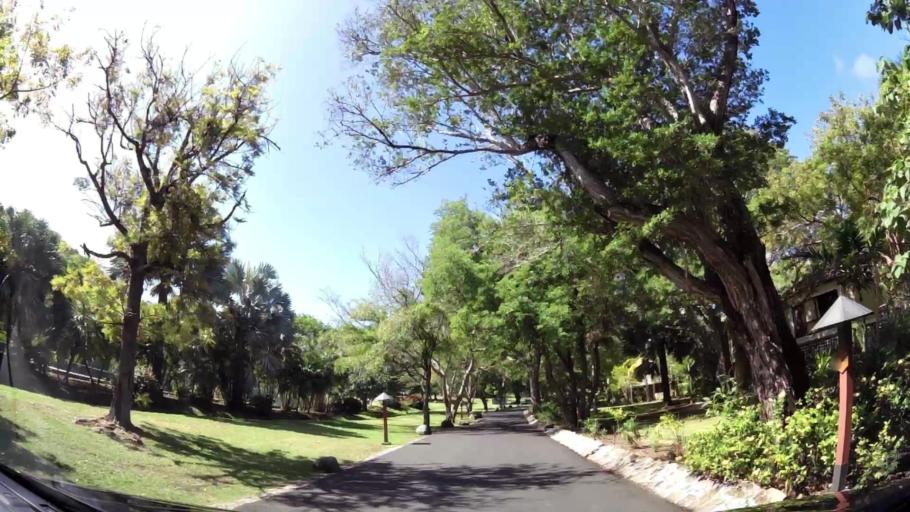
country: VG
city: Tortola
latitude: 18.4591
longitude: -64.4324
